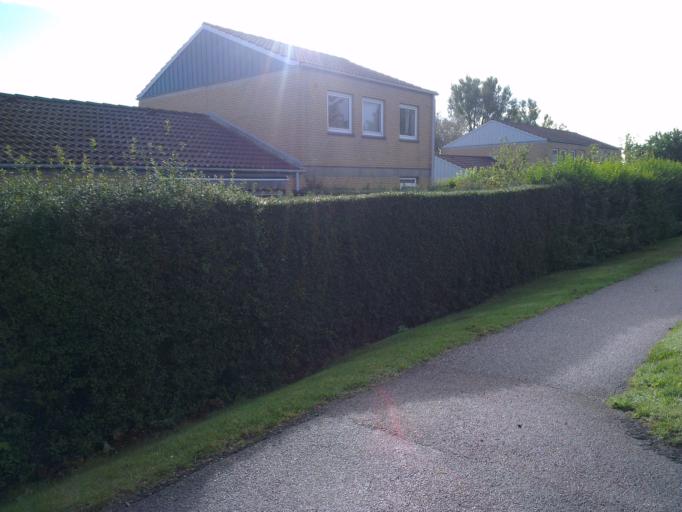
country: DK
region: Capital Region
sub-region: Frederikssund Kommune
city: Frederikssund
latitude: 55.8600
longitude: 12.0743
